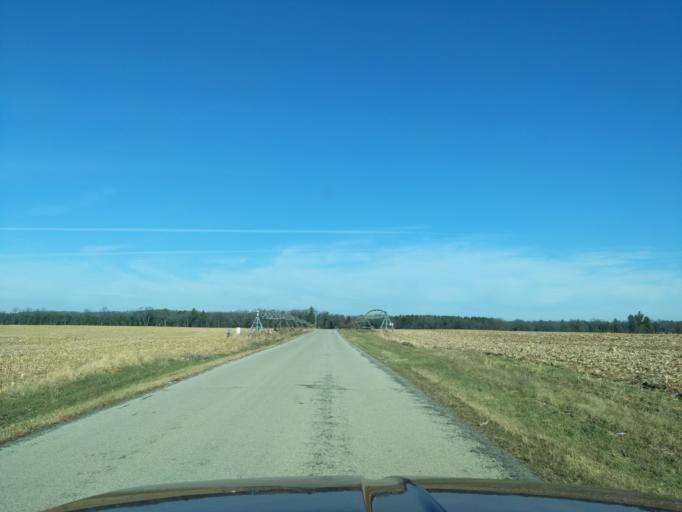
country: US
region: Wisconsin
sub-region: Waushara County
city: Silver Lake
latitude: 44.0933
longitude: -89.1739
